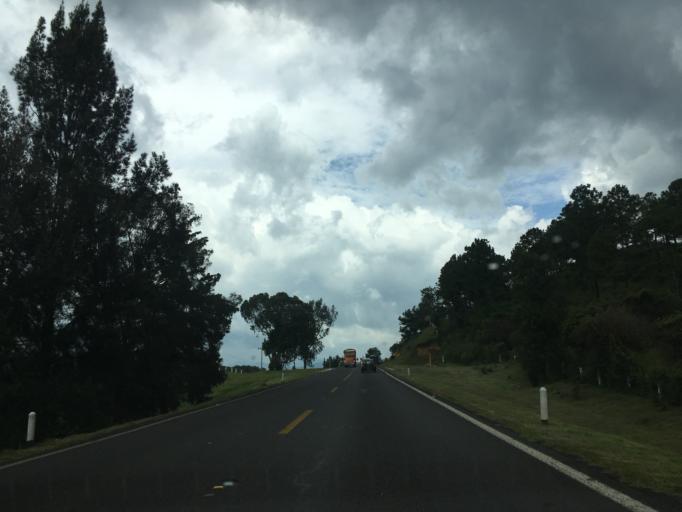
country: MX
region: Michoacan
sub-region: Patzcuaro
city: Santa Ana Chapitiro
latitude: 19.5319
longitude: -101.6356
